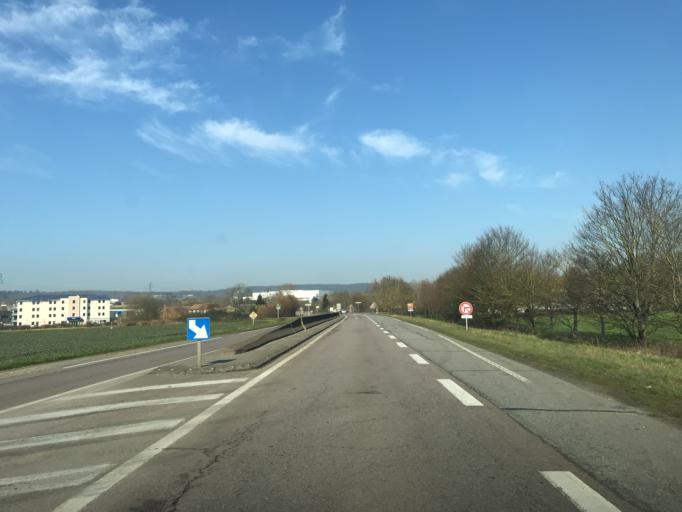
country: FR
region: Haute-Normandie
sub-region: Departement de l'Eure
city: Le Vaudreuil
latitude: 49.2471
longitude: 1.1912
